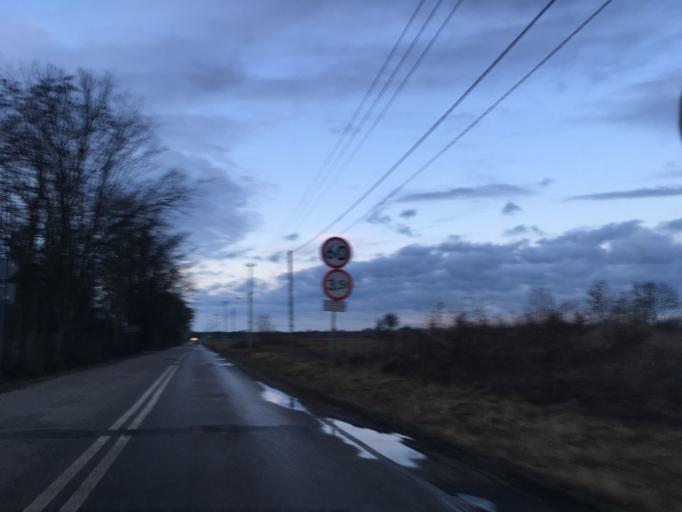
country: PL
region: Masovian Voivodeship
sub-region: Powiat pruszkowski
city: Owczarnia
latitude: 52.0844
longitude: 20.7098
